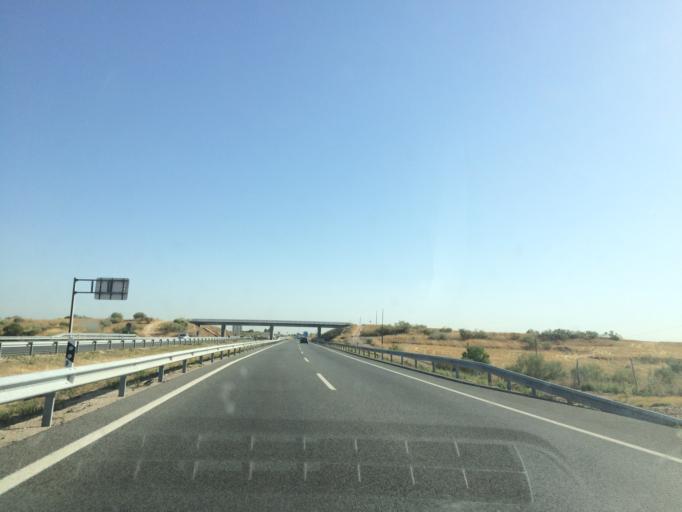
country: ES
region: Castille-La Mancha
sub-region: Province of Toledo
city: Valmojado
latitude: 40.2264
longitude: -4.0724
